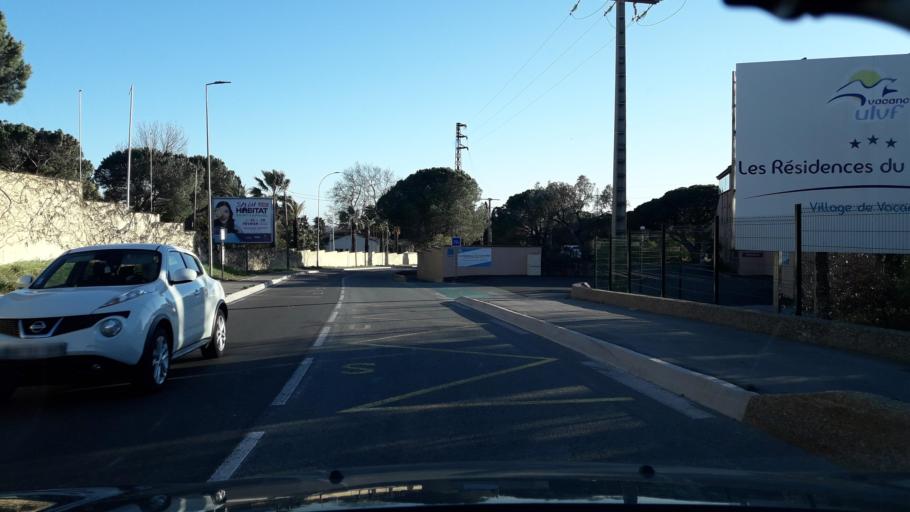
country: FR
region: Provence-Alpes-Cote d'Azur
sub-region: Departement du Var
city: Frejus
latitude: 43.4477
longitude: 6.7270
